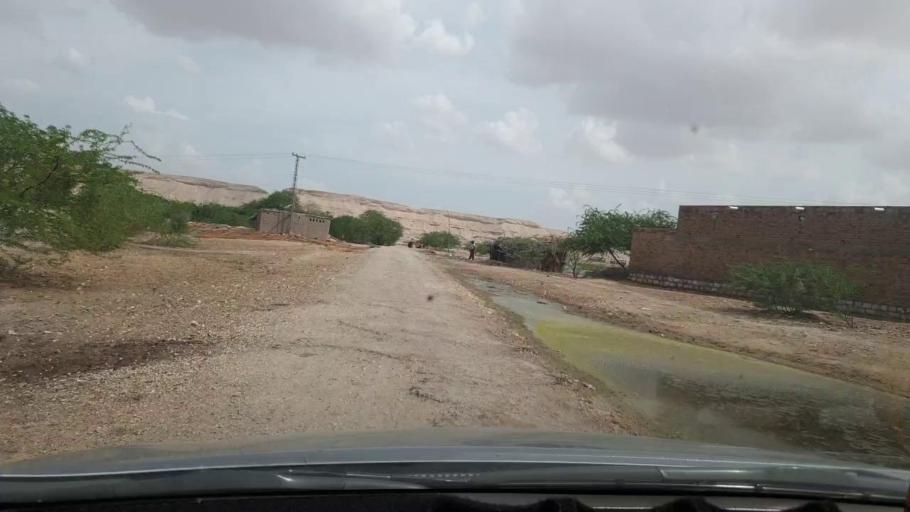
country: PK
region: Sindh
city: Khairpur
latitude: 27.4769
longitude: 68.8583
